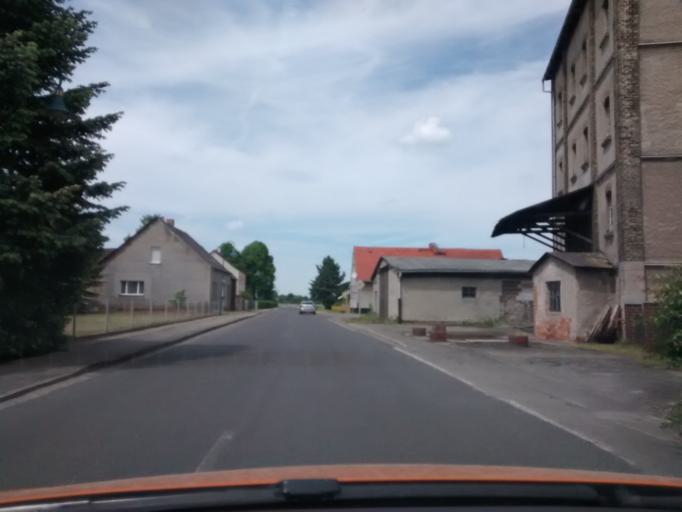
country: DE
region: Saxony-Anhalt
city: Holzdorf
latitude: 51.8428
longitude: 13.2184
